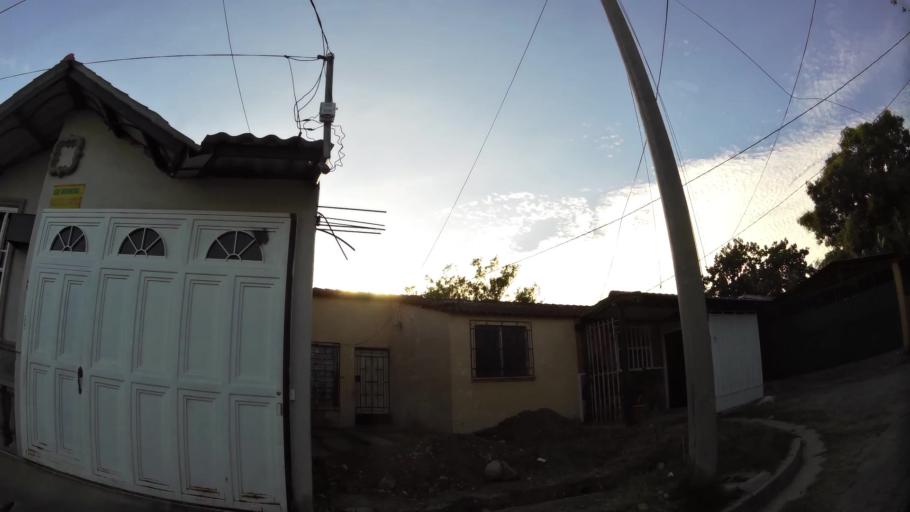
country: SV
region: Santa Ana
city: Metapan
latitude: 14.3329
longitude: -89.4527
